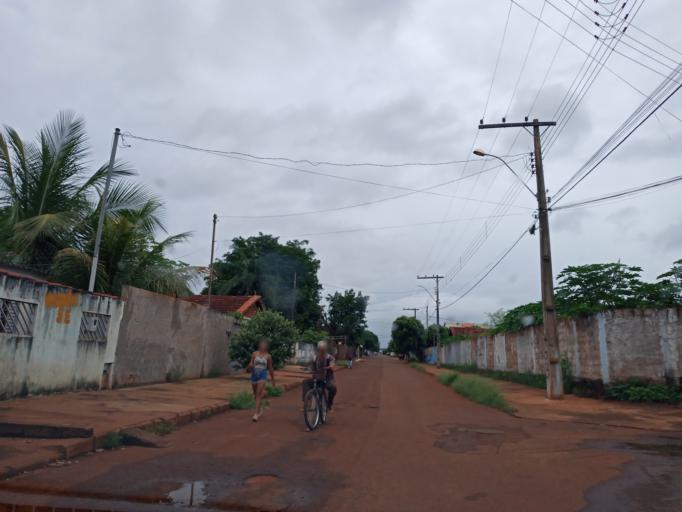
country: BR
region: Minas Gerais
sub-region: Centralina
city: Centralina
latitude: -18.5833
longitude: -49.2061
